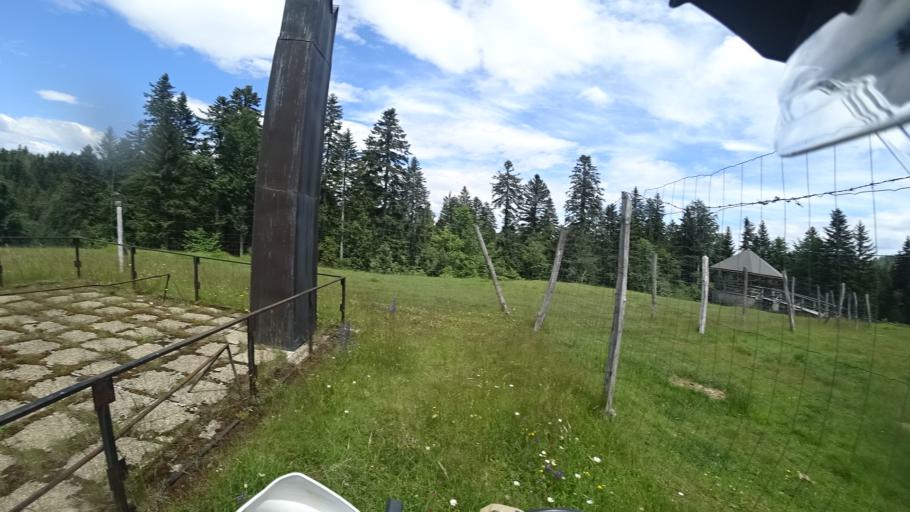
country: SI
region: Loska Dolina
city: Leskova Dolina
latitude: 45.6009
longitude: 14.5581
